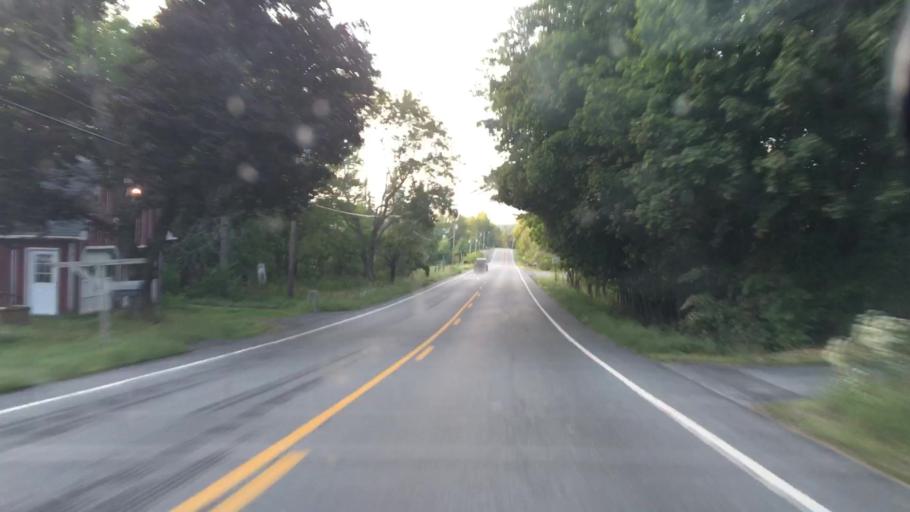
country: US
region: Maine
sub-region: Penobscot County
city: Hermon
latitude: 44.7355
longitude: -68.9641
